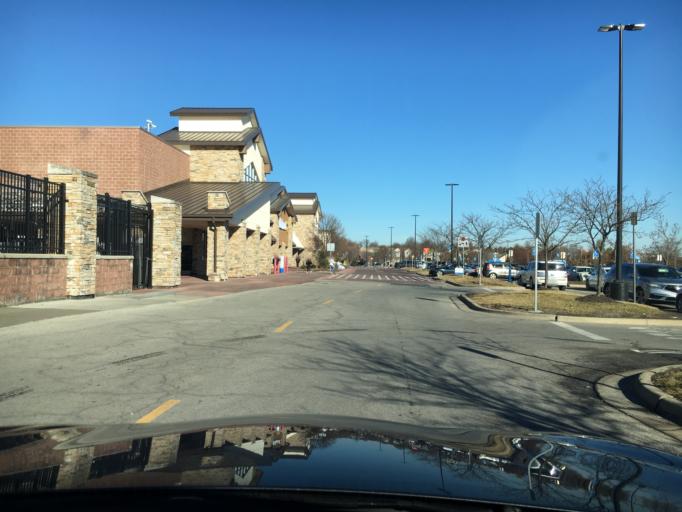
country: US
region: Kansas
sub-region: Johnson County
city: Lenexa
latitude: 38.8417
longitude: -94.6689
